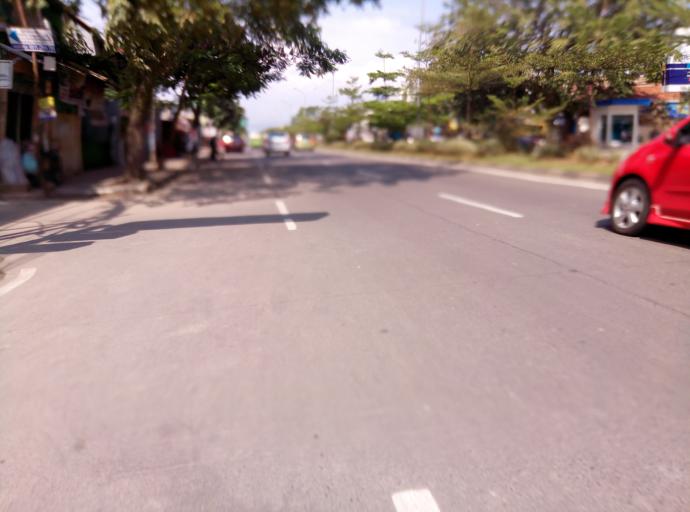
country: ID
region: West Java
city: Bandung
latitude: -6.9361
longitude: 107.6426
